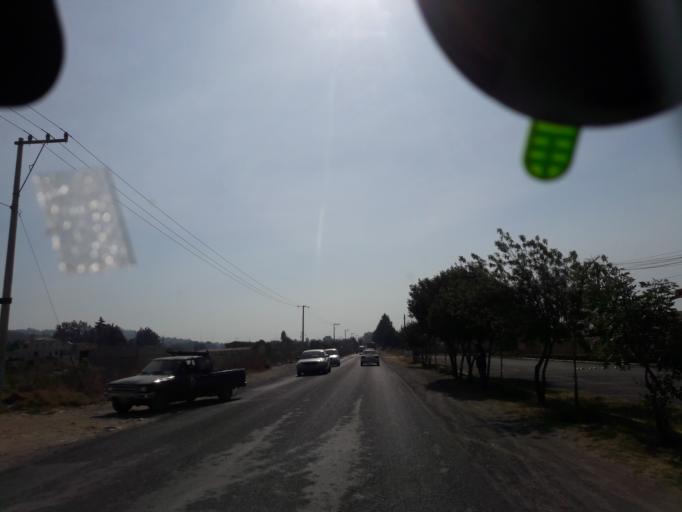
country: MX
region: Tlaxcala
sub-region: Panotla
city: Fraccionamiento la Virgen
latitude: 19.3204
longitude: -98.2875
